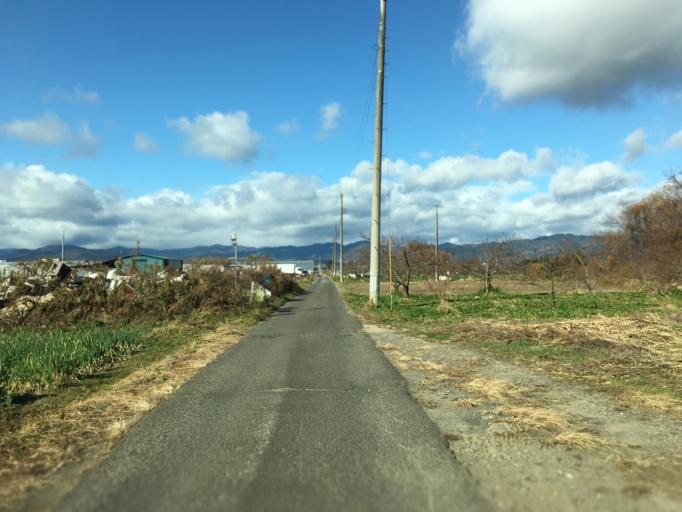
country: JP
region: Fukushima
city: Fukushima-shi
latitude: 37.7877
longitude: 140.4996
